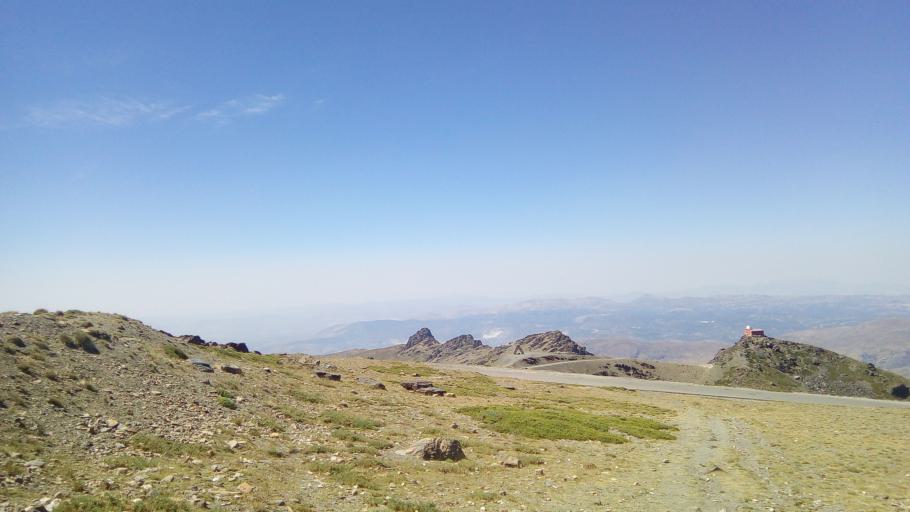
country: ES
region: Andalusia
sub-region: Provincia de Granada
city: Guejar-Sierra
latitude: 37.0849
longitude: -3.3808
